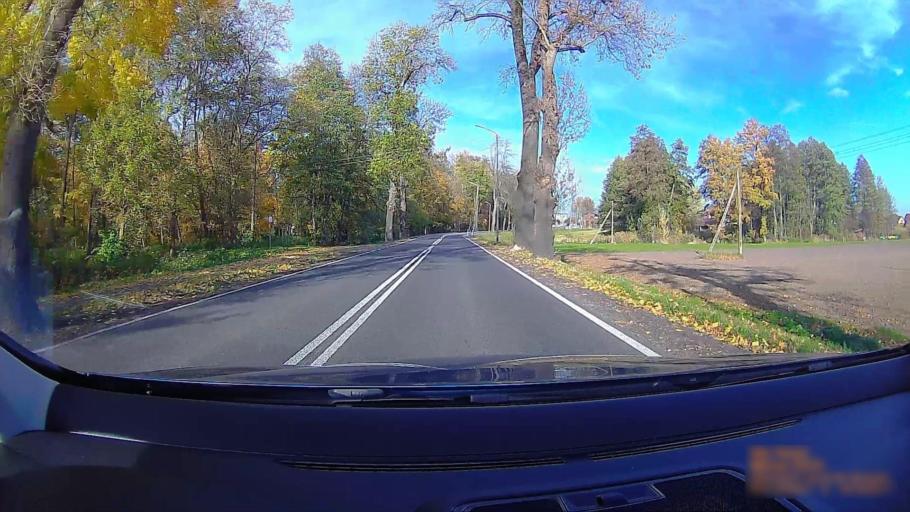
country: PL
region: Greater Poland Voivodeship
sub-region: Powiat ostrzeszowski
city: Doruchow
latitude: 51.4136
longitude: 18.0760
